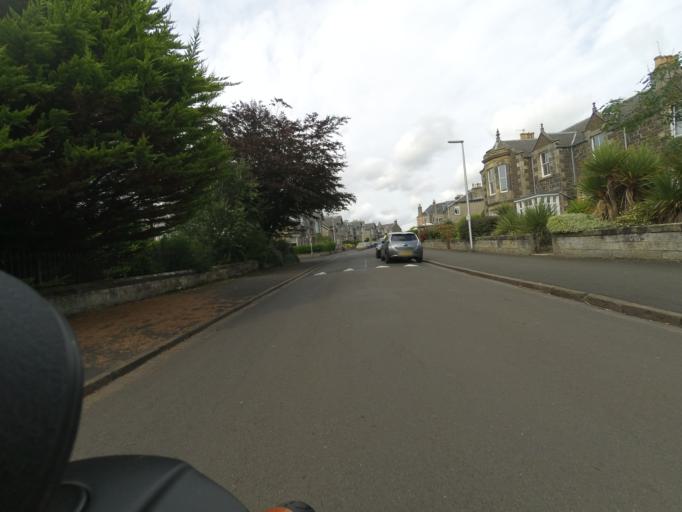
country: GB
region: Scotland
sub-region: Fife
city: Lundin Links
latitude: 56.2129
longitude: -2.9517
